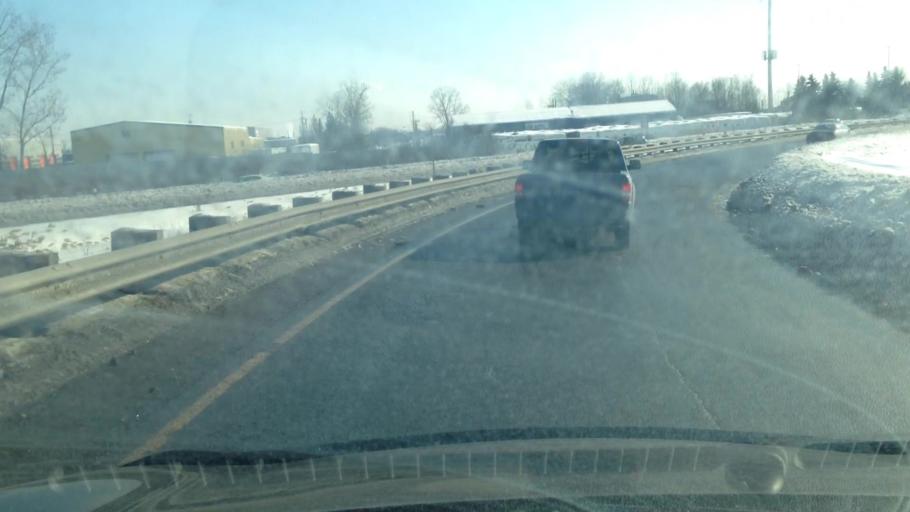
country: CA
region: Quebec
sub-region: Laurentides
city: Boisbriand
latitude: 45.6277
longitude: -73.8369
